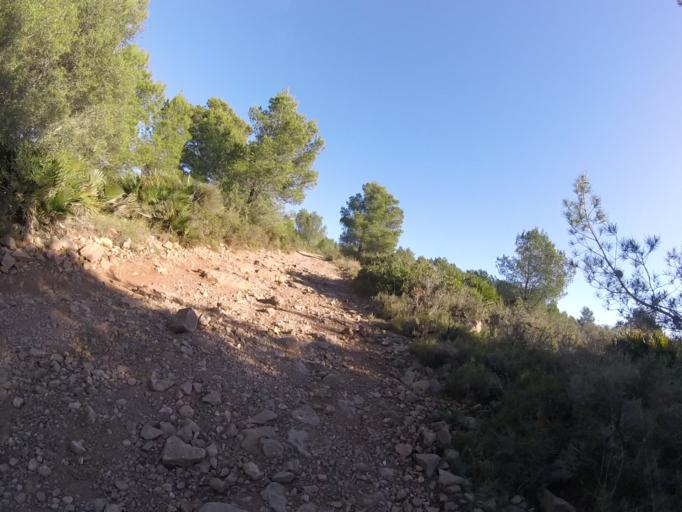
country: ES
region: Valencia
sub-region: Provincia de Castello
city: Benicassim
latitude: 40.0857
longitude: 0.0897
